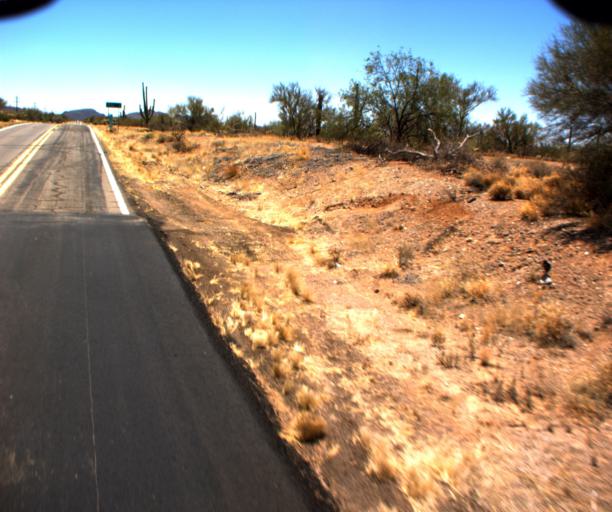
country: US
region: Arizona
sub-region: Pima County
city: Sells
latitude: 32.0067
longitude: -111.9906
